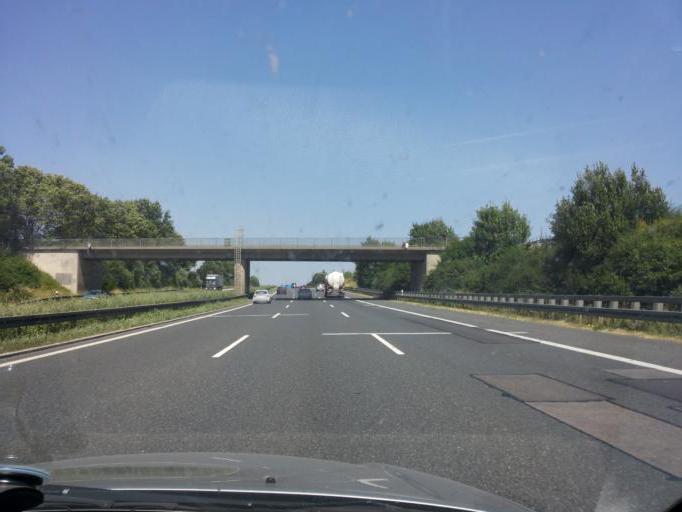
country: DE
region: Bavaria
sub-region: Upper Bavaria
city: Denkendorf
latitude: 48.9172
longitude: 11.4697
